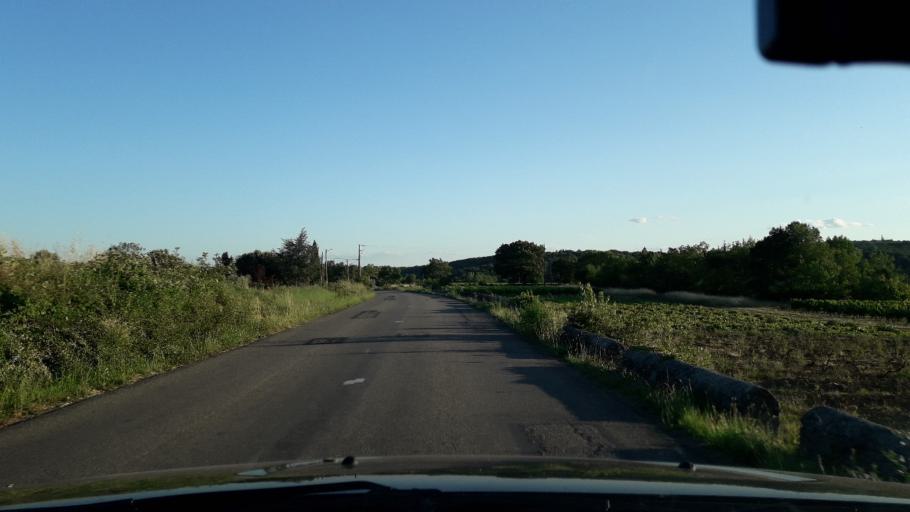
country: FR
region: Rhone-Alpes
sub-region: Departement de l'Ardeche
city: Lavilledieu
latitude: 44.6002
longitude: 4.4643
